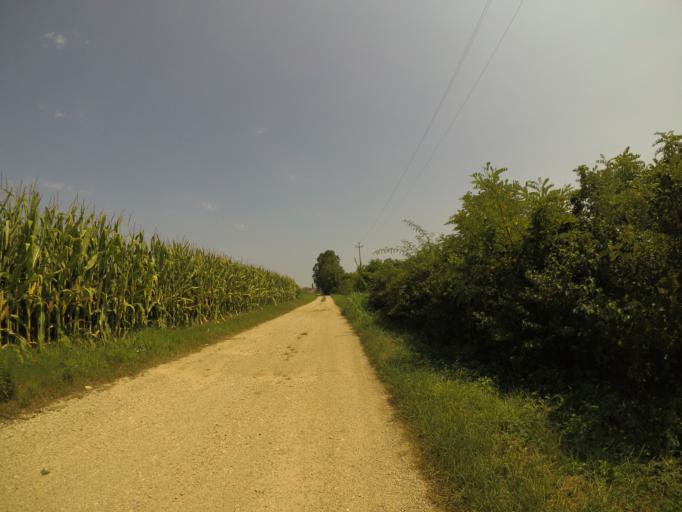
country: IT
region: Friuli Venezia Giulia
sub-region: Provincia di Udine
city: Lestizza
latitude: 45.9504
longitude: 13.1320
